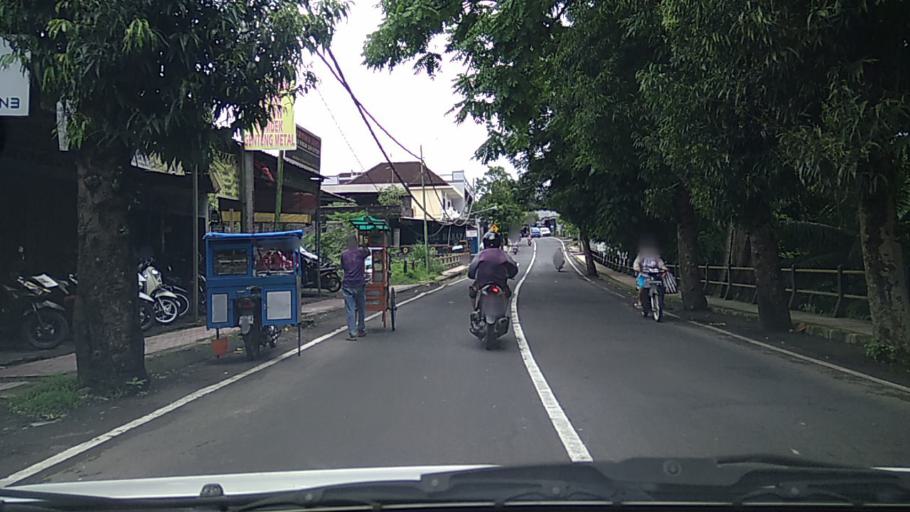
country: ID
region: Bali
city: Banjar Kelodan
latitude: -8.5408
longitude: 115.3354
